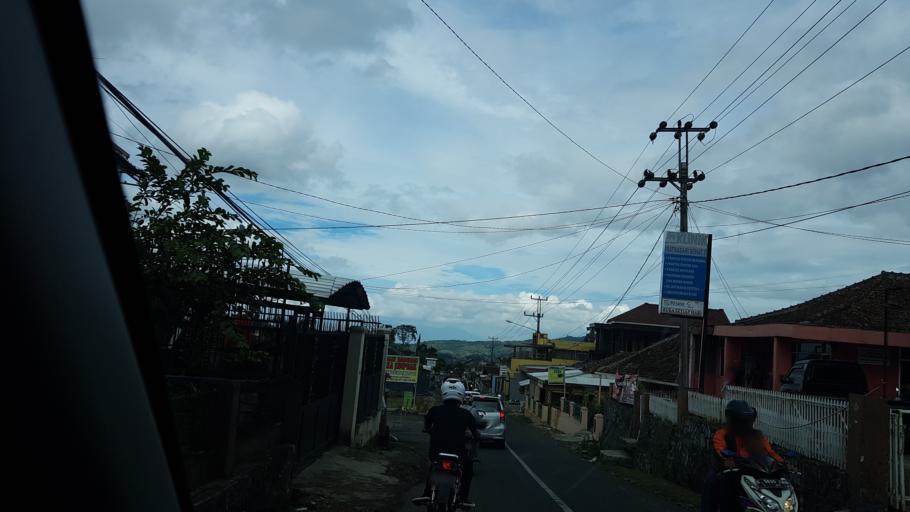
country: ID
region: West Java
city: Banjar
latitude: -7.1098
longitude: 107.4522
